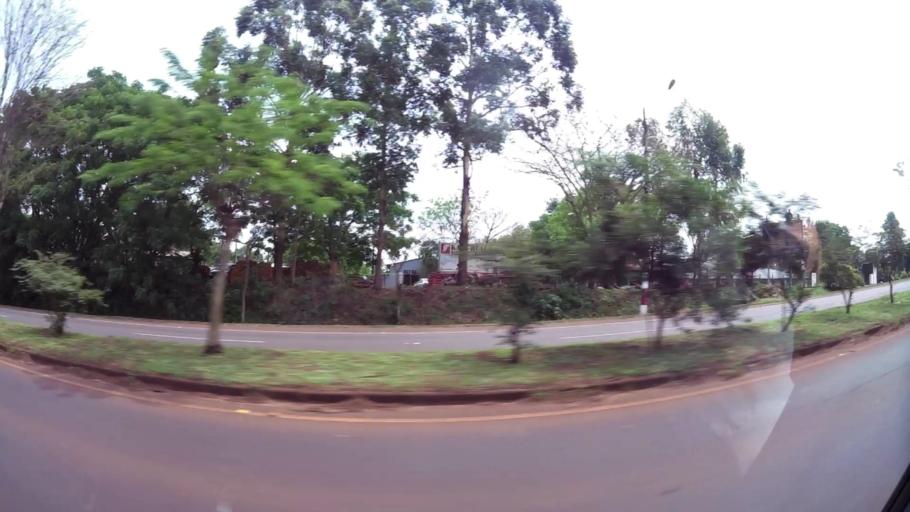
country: PY
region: Alto Parana
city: Ciudad del Este
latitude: -25.4859
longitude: -54.6282
